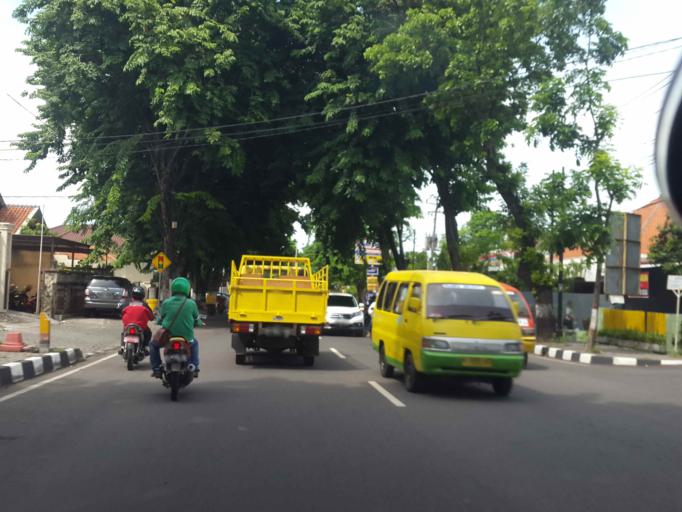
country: ID
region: Central Java
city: Semarang
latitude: -6.9887
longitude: 110.3825
